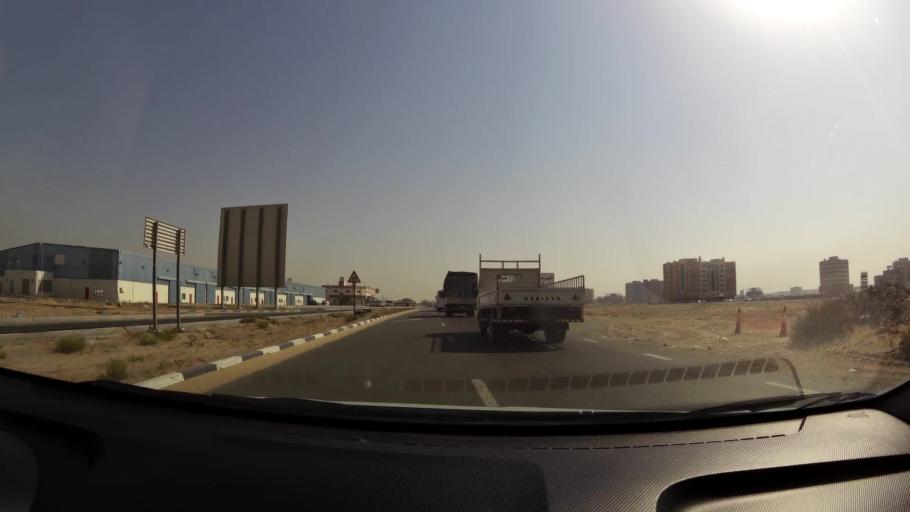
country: AE
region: Ajman
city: Ajman
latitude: 25.4237
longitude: 55.5316
